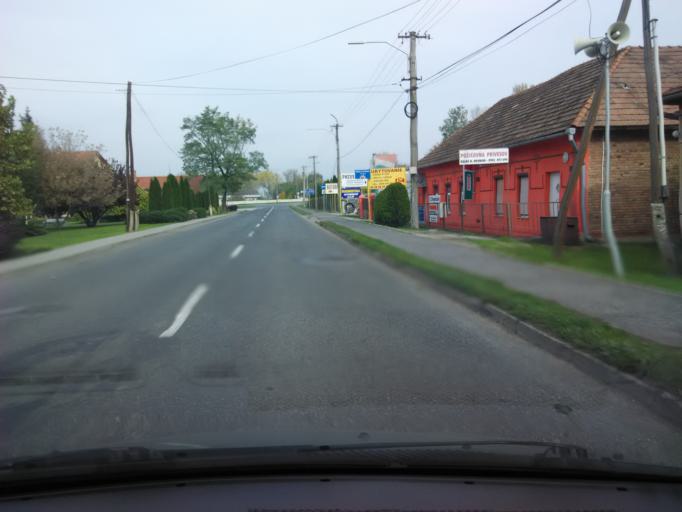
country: SK
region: Nitriansky
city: Levice
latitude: 48.2011
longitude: 18.5208
